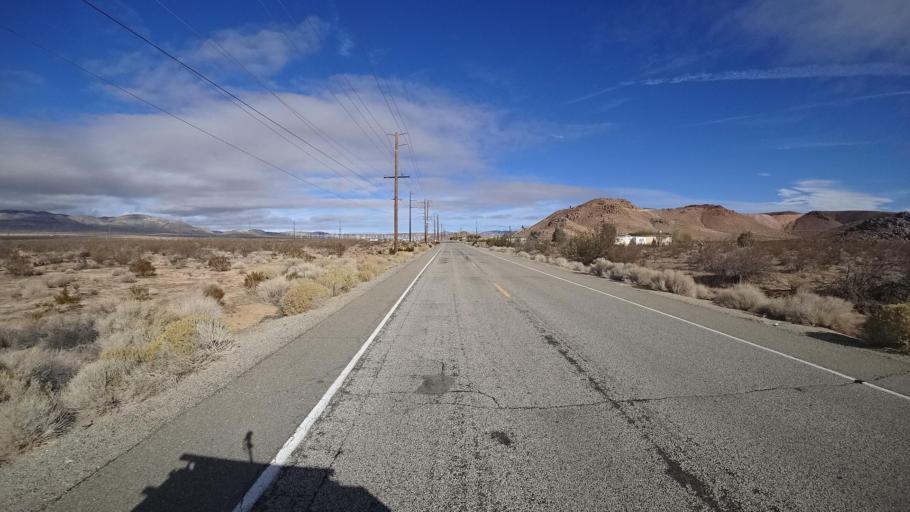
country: US
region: California
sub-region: Kern County
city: Rosamond
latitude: 34.9484
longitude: -118.2917
